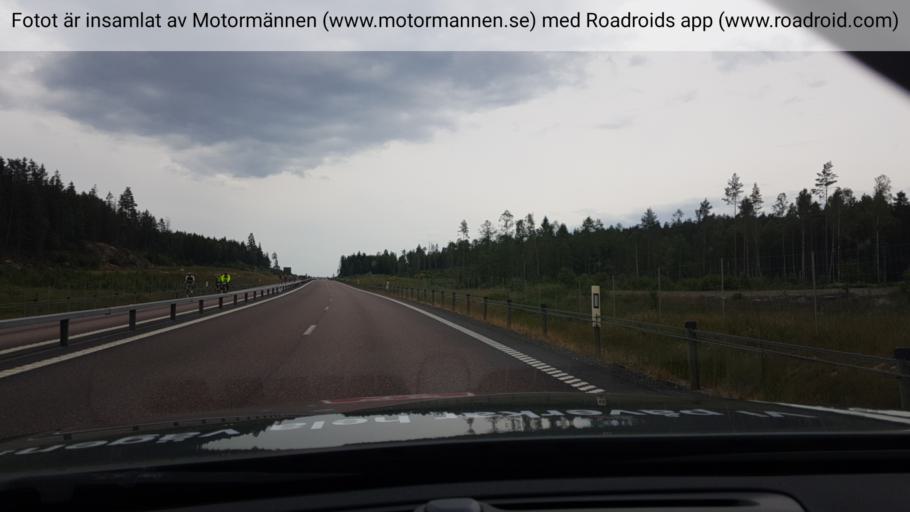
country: SE
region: OErebro
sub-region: Askersunds Kommun
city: Askersund
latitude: 58.8470
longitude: 14.9068
